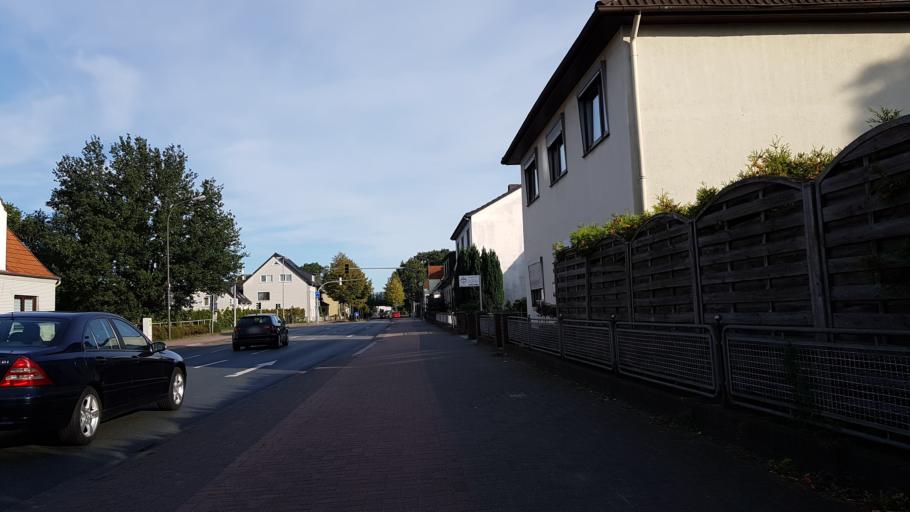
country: DE
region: Lower Saxony
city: Oyten
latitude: 53.0325
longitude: 8.9585
